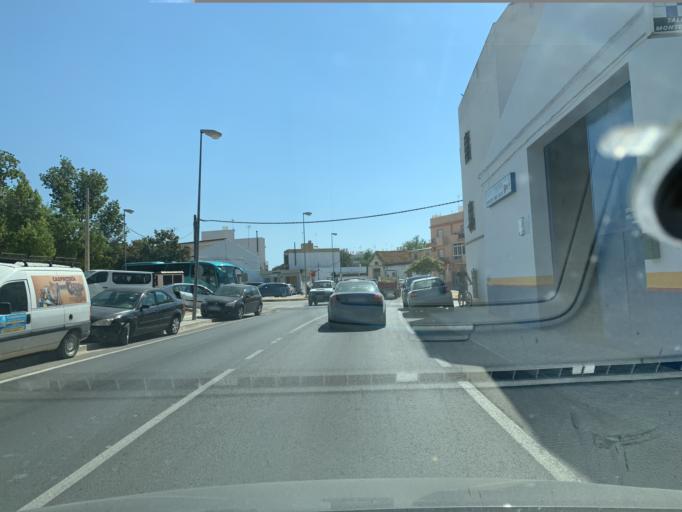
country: ES
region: Andalusia
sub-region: Provincia de Sevilla
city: Marchena
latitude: 37.3305
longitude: -5.4103
